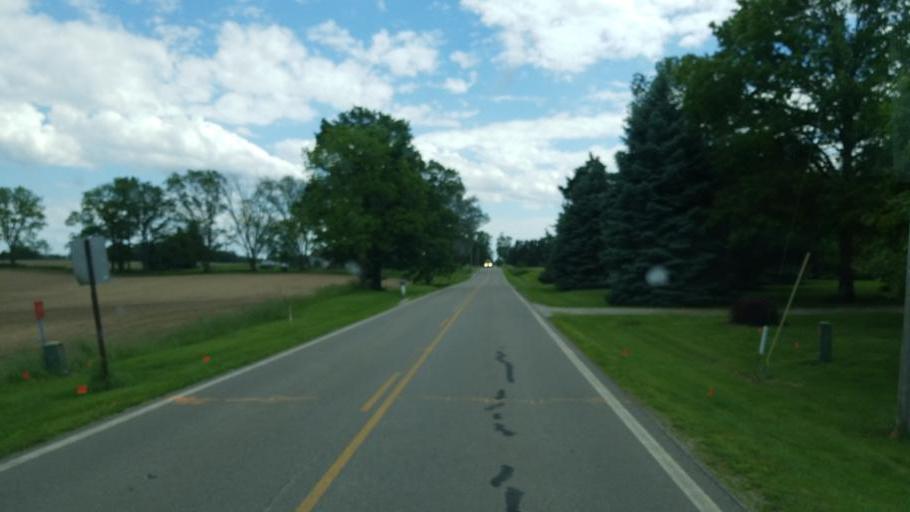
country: US
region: Ohio
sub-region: Huron County
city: Plymouth
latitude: 41.0954
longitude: -82.6113
